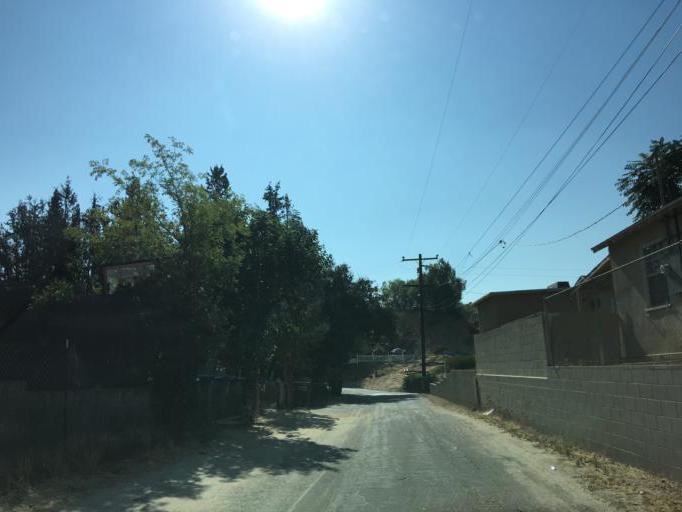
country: US
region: California
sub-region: Los Angeles County
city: Val Verde
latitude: 34.4485
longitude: -118.6613
